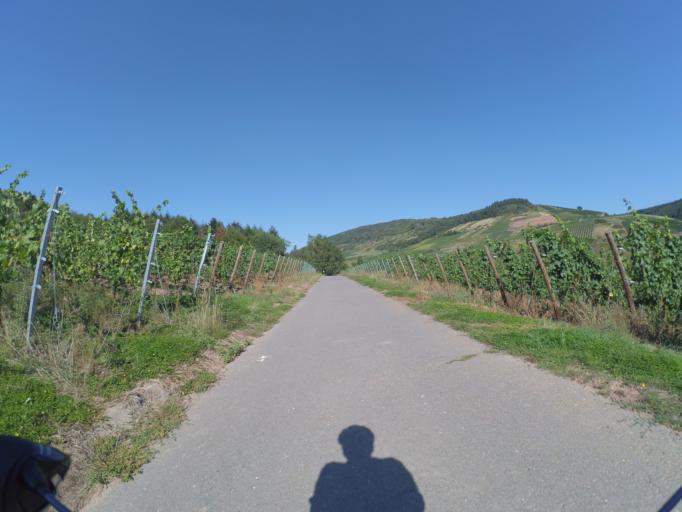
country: DE
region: Rheinland-Pfalz
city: Rivenich
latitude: 49.8656
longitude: 6.8465
